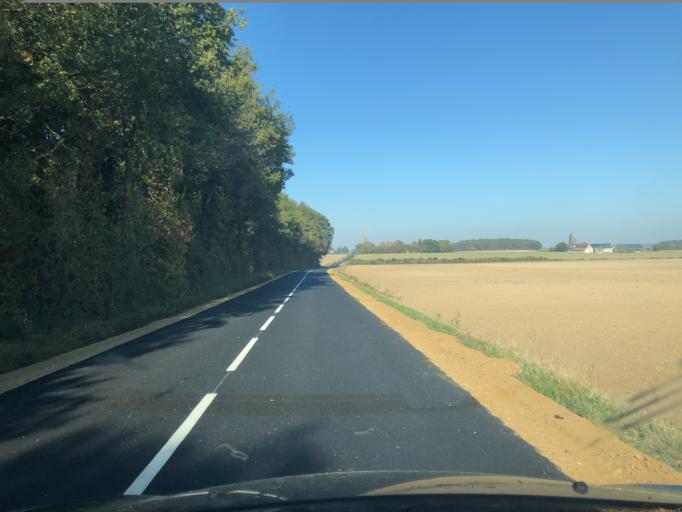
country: FR
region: Centre
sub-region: Departement d'Indre-et-Loire
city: Neuvy-le-Roi
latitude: 47.5545
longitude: 0.6116
